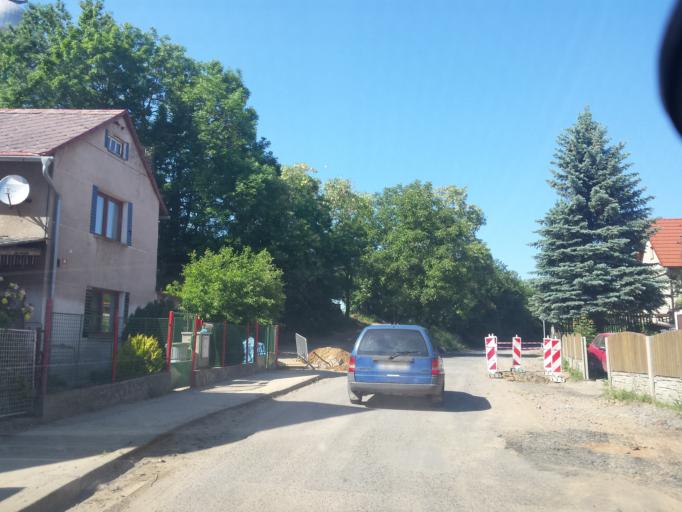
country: CZ
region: Central Bohemia
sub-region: Okres Melnik
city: Melnik
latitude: 50.4138
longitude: 14.5396
